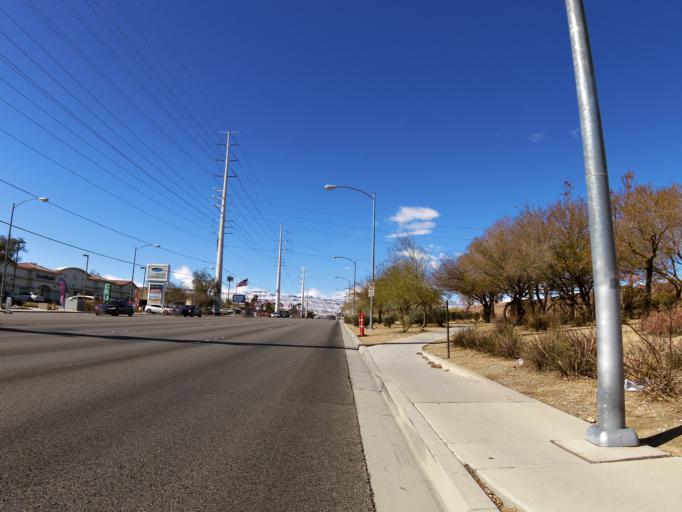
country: US
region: Nevada
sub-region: Clark County
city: Spring Valley
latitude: 36.1149
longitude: -115.2745
